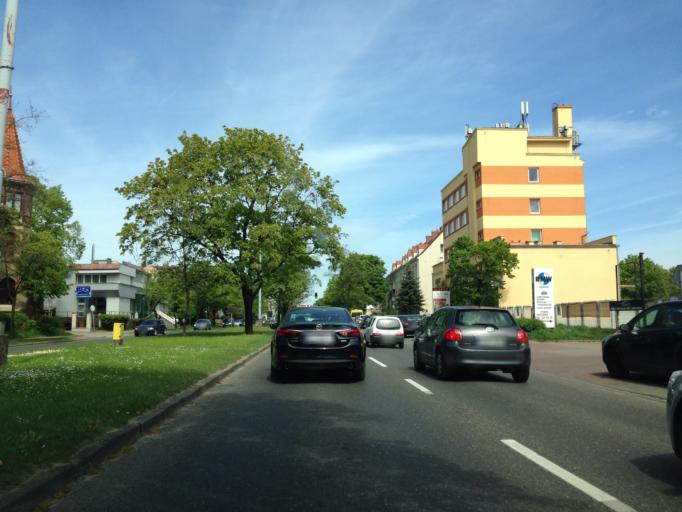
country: PL
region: Pomeranian Voivodeship
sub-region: Sopot
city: Sopot
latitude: 54.4261
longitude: 18.5630
